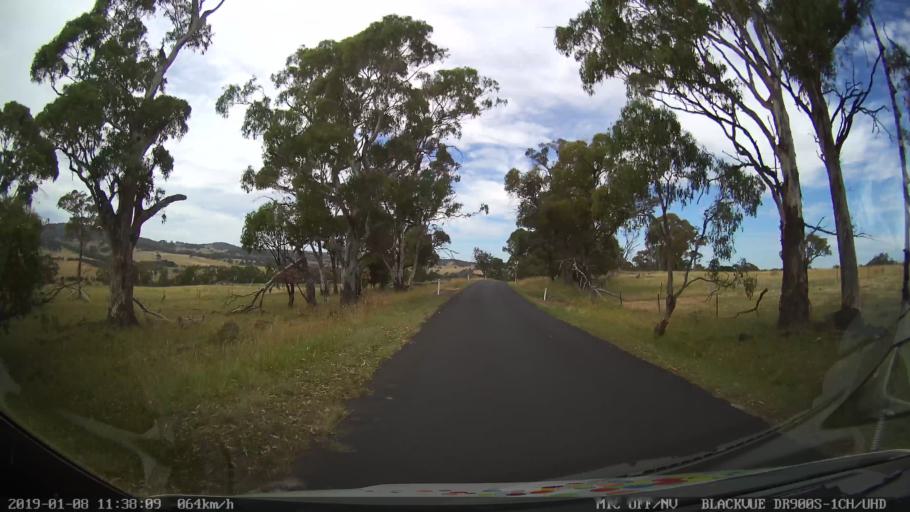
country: AU
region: New South Wales
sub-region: Guyra
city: Guyra
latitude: -30.3579
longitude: 151.5554
